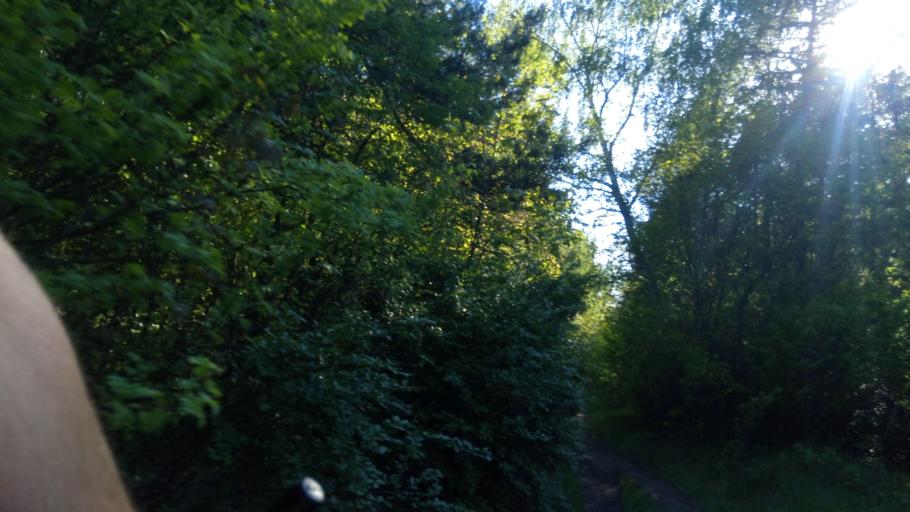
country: RU
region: Chelyabinsk
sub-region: Gorod Chelyabinsk
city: Chelyabinsk
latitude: 55.1438
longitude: 61.3452
